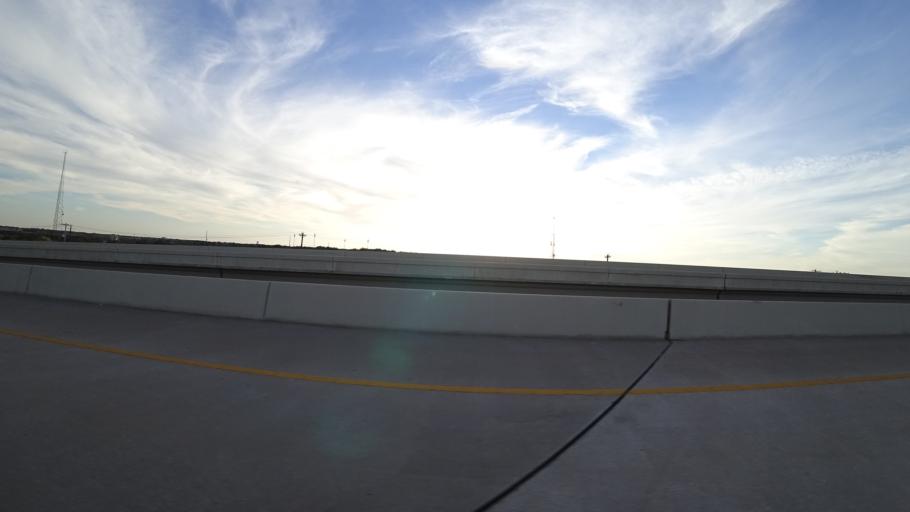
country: US
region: Texas
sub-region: Williamson County
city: Cedar Park
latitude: 30.5020
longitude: -97.8076
